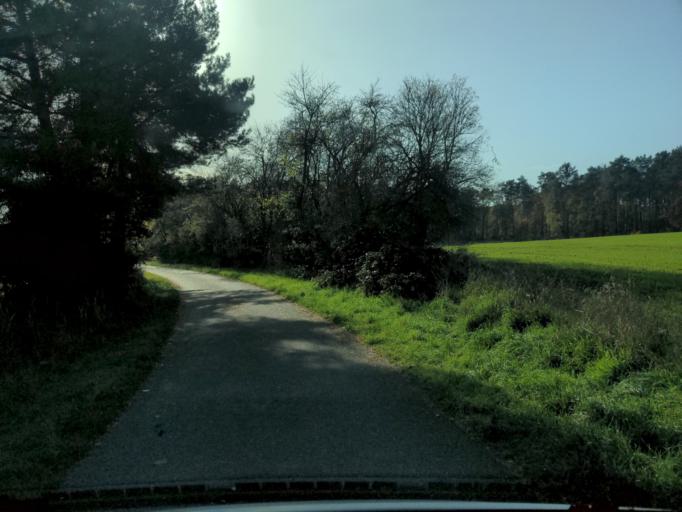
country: DE
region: Brandenburg
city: Cottbus
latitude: 51.6794
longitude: 14.3365
